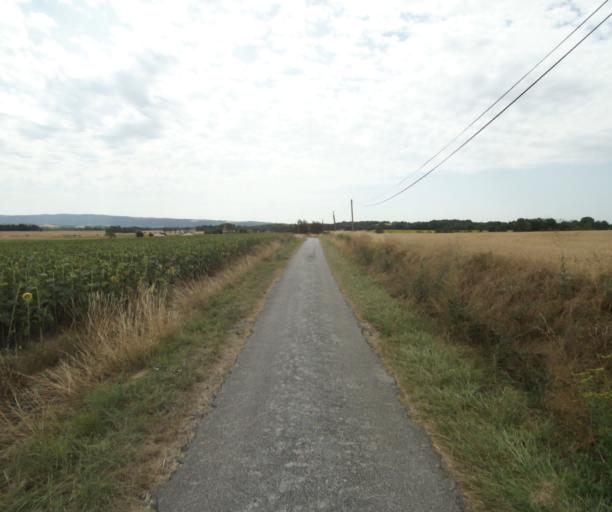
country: FR
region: Midi-Pyrenees
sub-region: Departement de la Haute-Garonne
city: Saint-Felix-Lauragais
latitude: 43.4390
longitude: 1.9126
